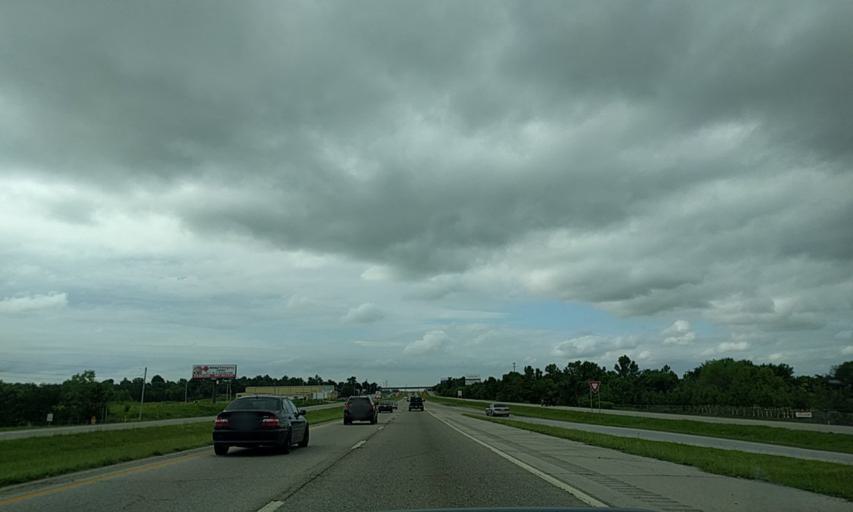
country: US
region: Oklahoma
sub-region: Tulsa County
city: Owasso
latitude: 36.2618
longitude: -95.8482
